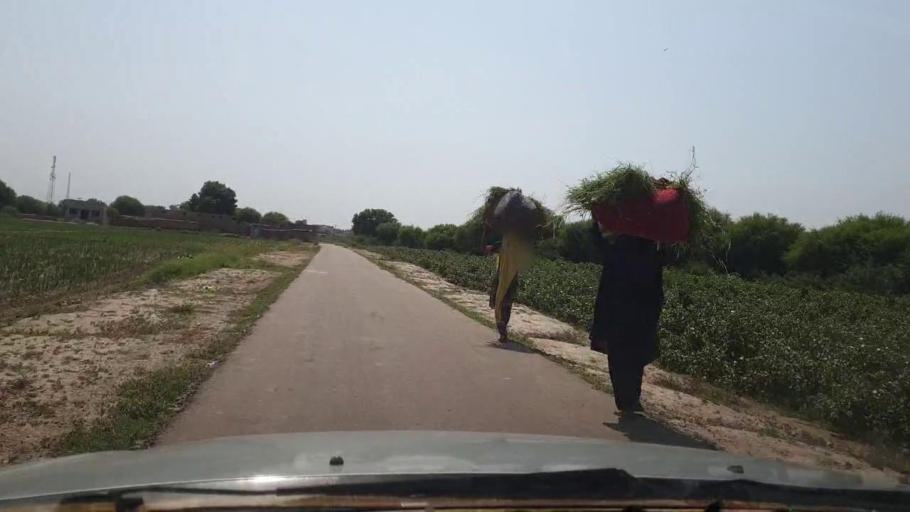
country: PK
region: Sindh
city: Chambar
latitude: 25.2230
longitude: 68.7781
